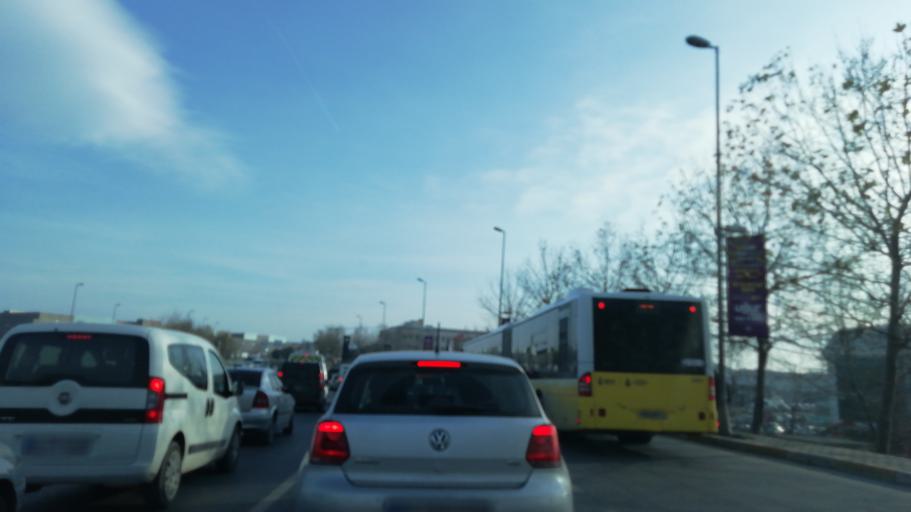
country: TR
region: Istanbul
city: Esenyurt
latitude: 41.0525
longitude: 28.6705
